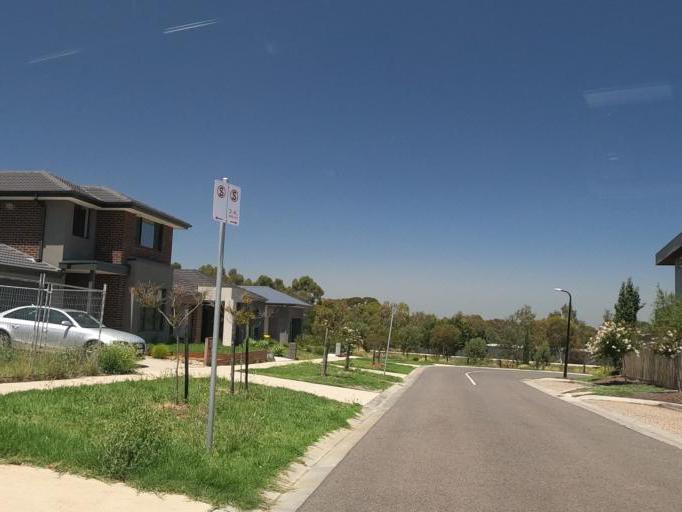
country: AU
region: Victoria
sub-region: Hume
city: Greenvale
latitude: -37.6255
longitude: 144.8926
